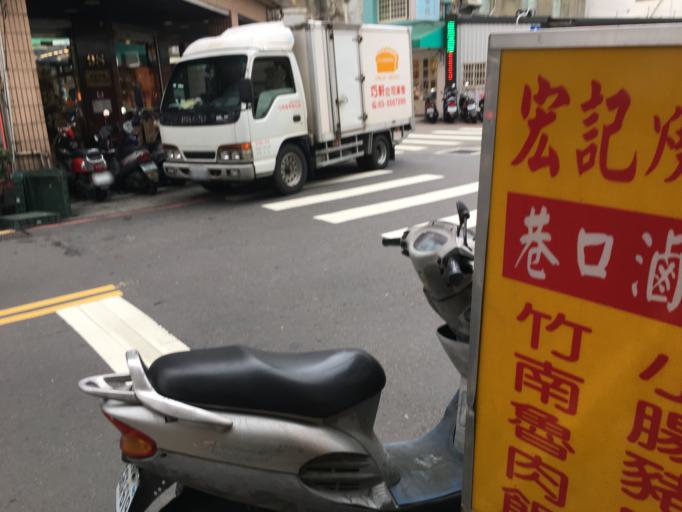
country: TW
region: Taiwan
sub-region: Hsinchu
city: Hsinchu
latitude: 24.8018
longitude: 120.9640
